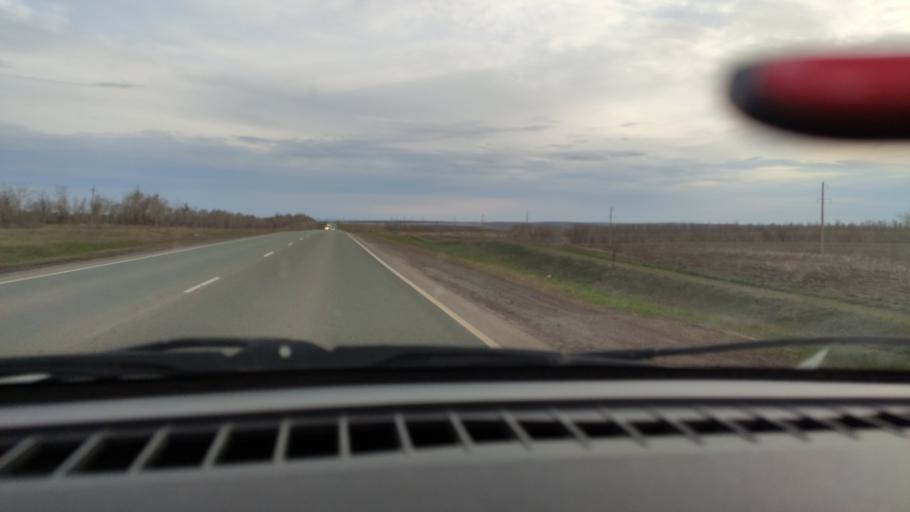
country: RU
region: Orenburg
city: Sakmara
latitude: 52.0524
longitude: 55.2552
